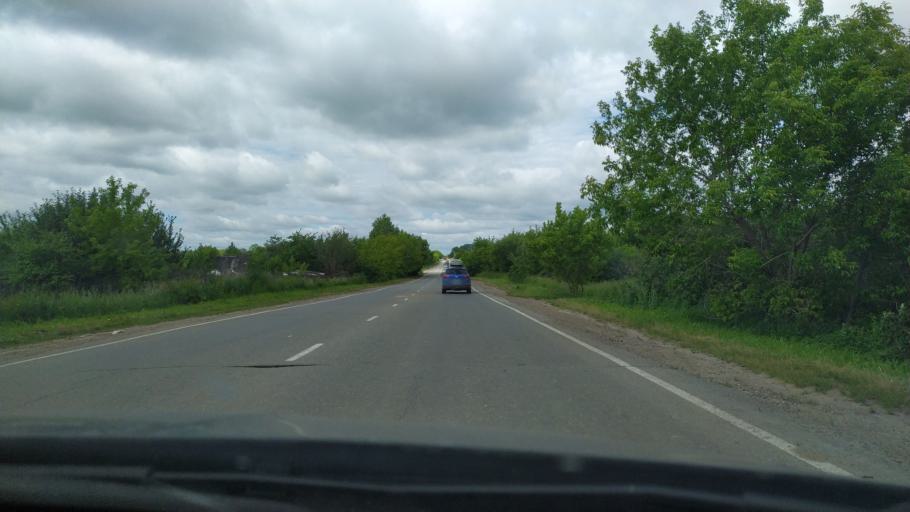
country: RU
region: Perm
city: Kondratovo
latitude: 57.9294
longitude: 56.1039
